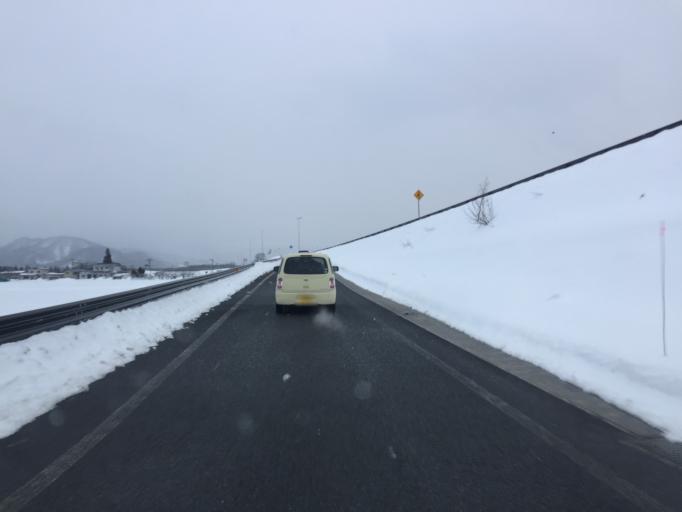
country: JP
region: Yamagata
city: Yonezawa
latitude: 37.9216
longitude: 140.1358
